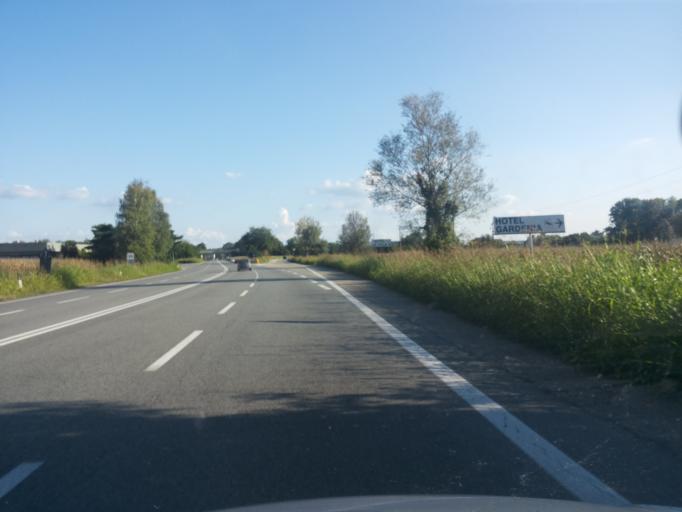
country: IT
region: Piedmont
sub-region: Provincia di Torino
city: Pavone Canavese
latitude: 45.4337
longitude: 7.8854
